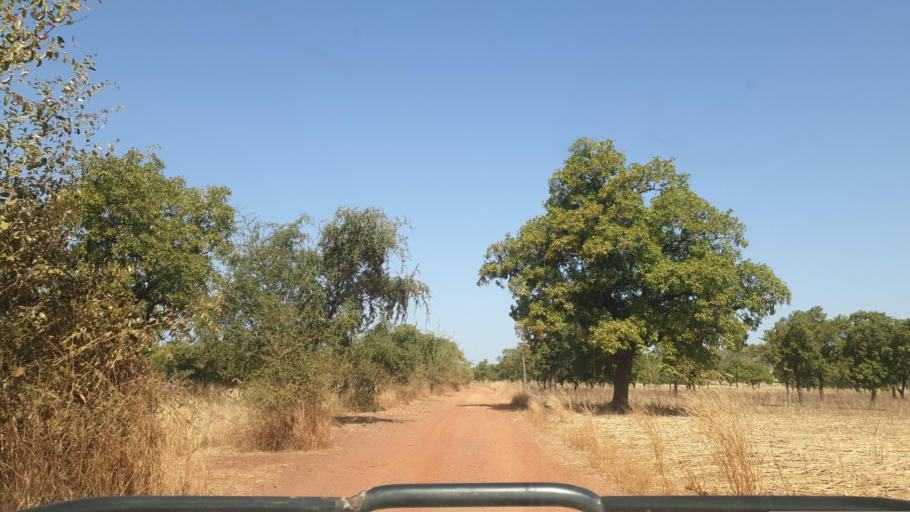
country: ML
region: Koulikoro
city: Dioila
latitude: 11.9038
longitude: -6.9825
